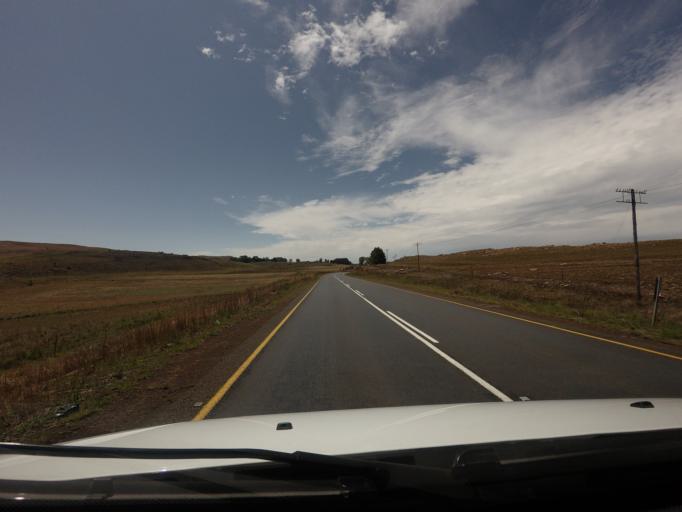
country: ZA
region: Mpumalanga
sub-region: Nkangala District Municipality
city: Belfast
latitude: -25.3830
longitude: 30.1340
